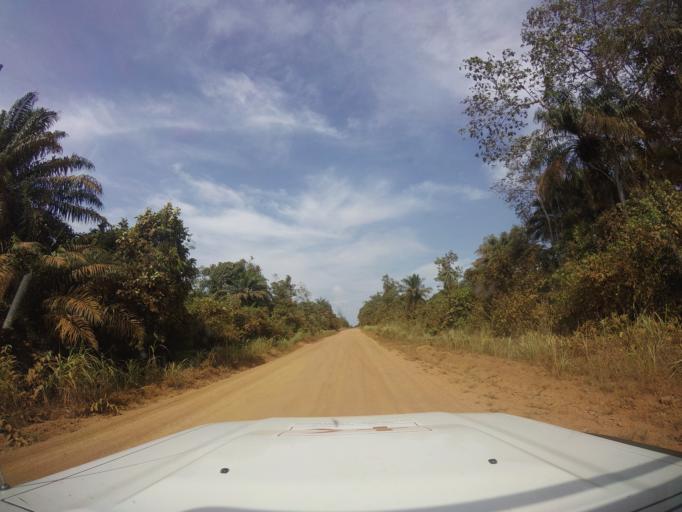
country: LR
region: Grand Cape Mount
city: Robertsport
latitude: 6.6818
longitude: -11.1316
